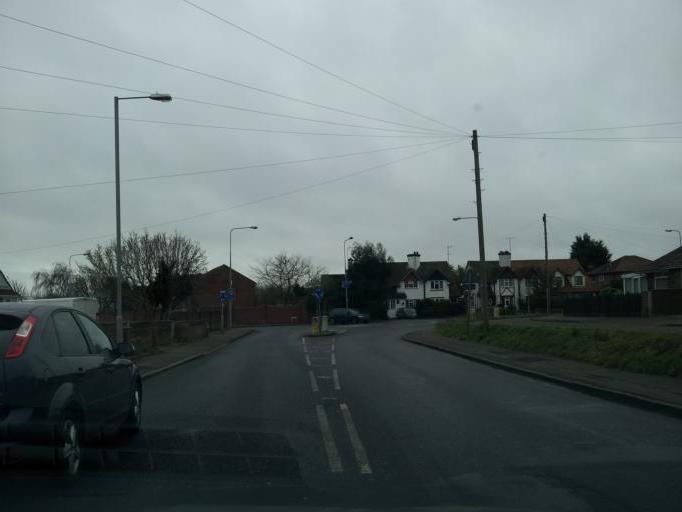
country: GB
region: England
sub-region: Essex
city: Dovercourt
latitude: 51.9290
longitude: 1.2438
